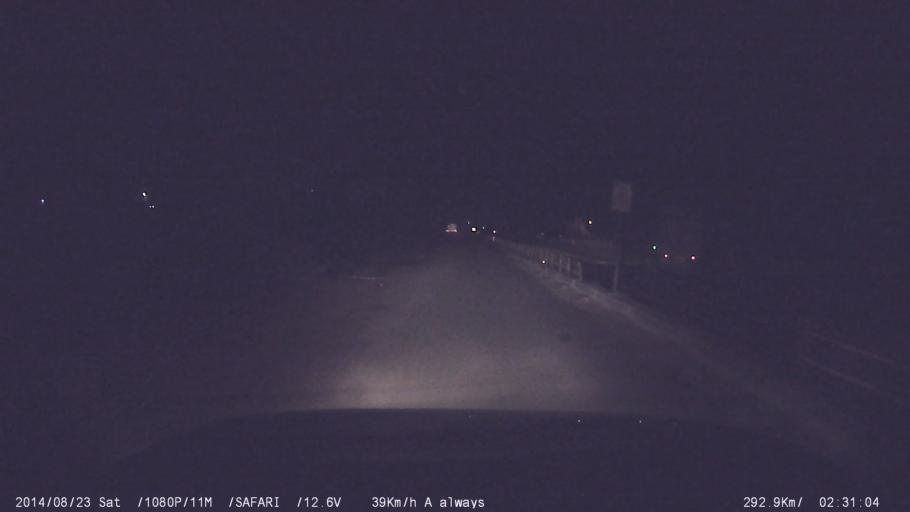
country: IN
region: Tamil Nadu
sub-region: Kancheepuram
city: Sriperumbudur
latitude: 12.9633
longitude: 79.9471
